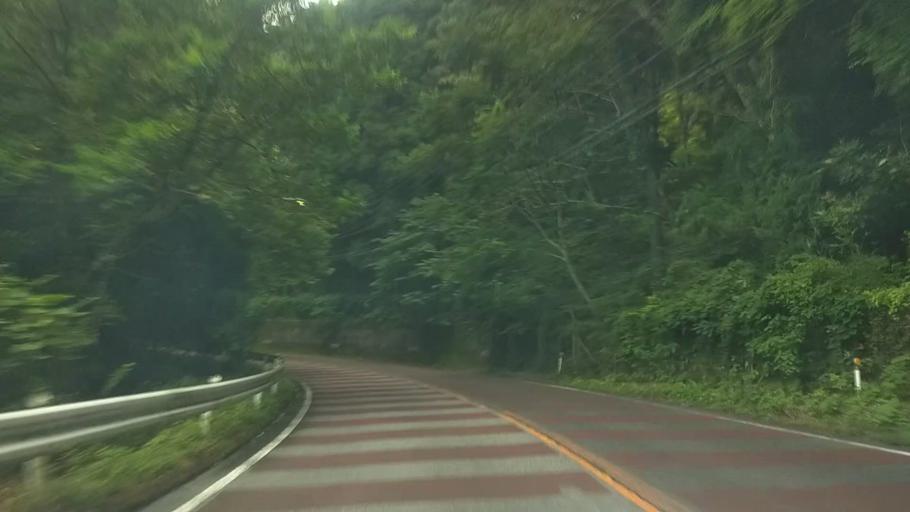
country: JP
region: Chiba
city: Kawaguchi
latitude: 35.2082
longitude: 140.0672
